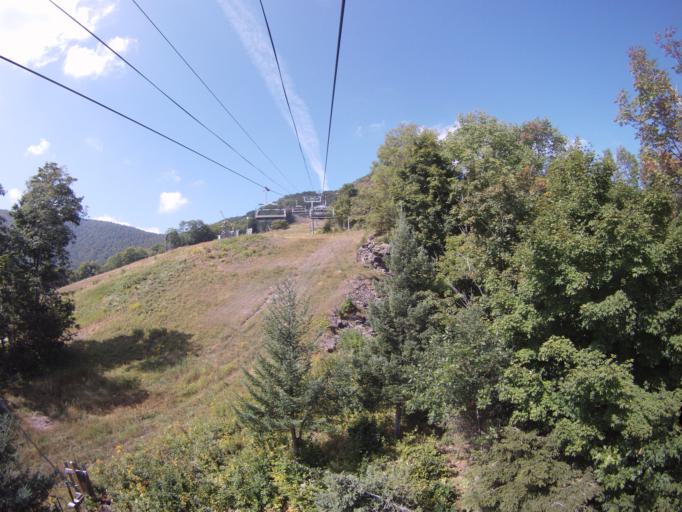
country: US
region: New York
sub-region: Ulster County
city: Woodstock
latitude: 42.2028
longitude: -74.2214
